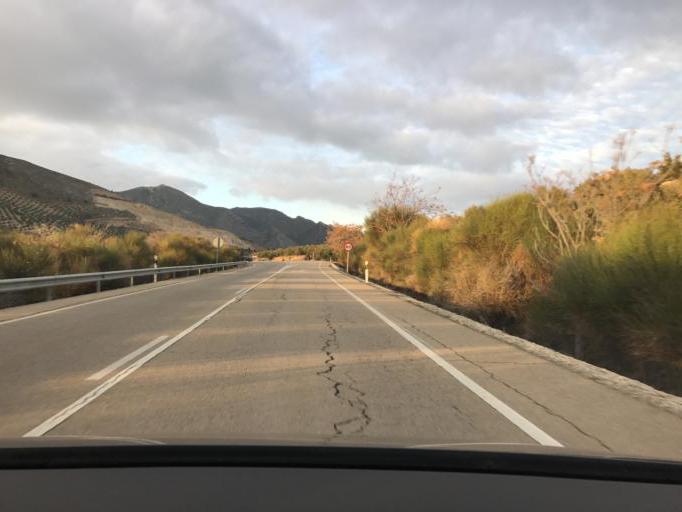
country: ES
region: Andalusia
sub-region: Provincia de Jaen
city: Jodar
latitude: 37.8122
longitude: -3.3696
